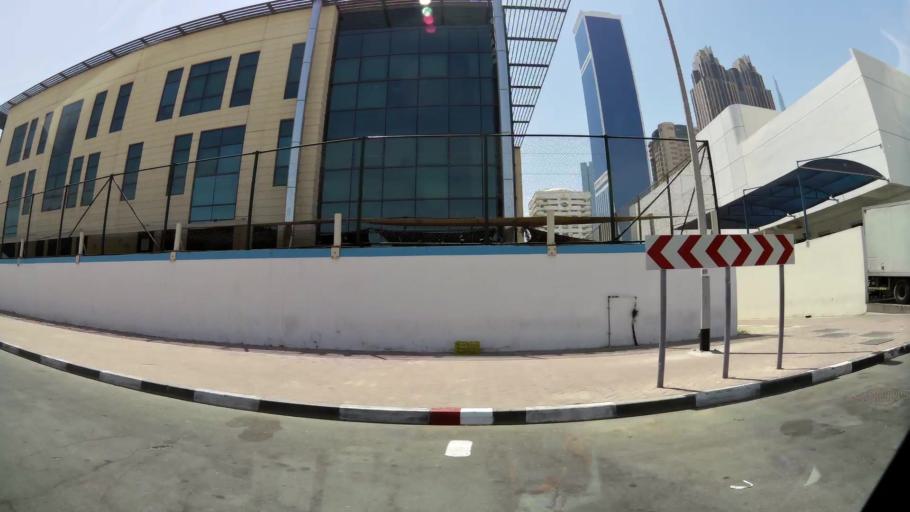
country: AE
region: Dubai
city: Dubai
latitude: 25.2111
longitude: 55.2707
